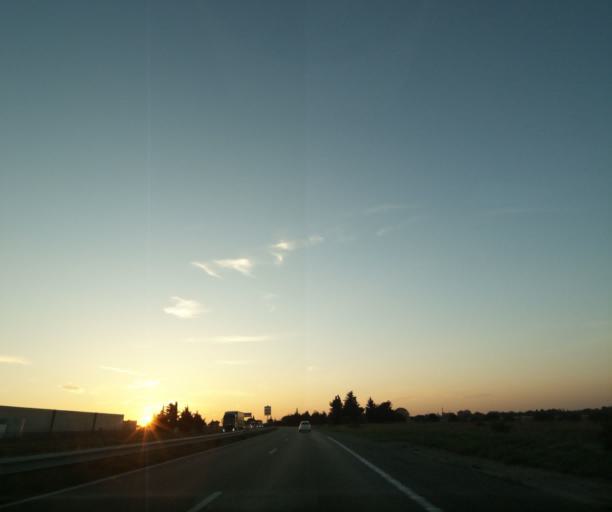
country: FR
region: Provence-Alpes-Cote d'Azur
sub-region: Departement des Bouches-du-Rhone
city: Saint-Martin-de-Crau
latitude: 43.6339
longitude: 4.7793
